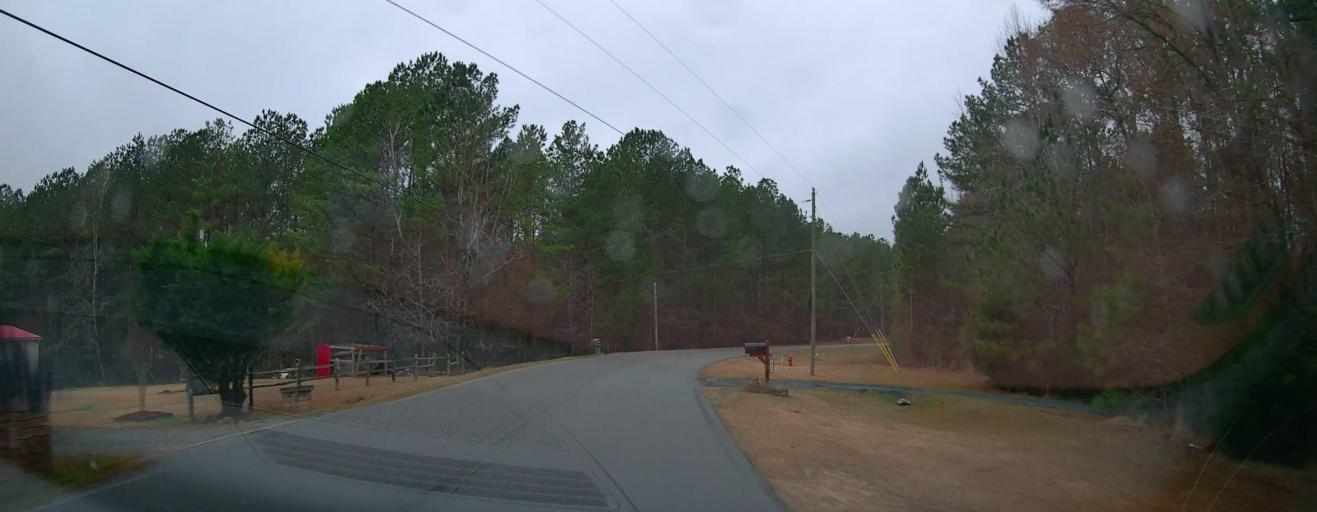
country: US
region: Georgia
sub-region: Monroe County
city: Forsyth
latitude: 33.0845
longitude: -83.9182
